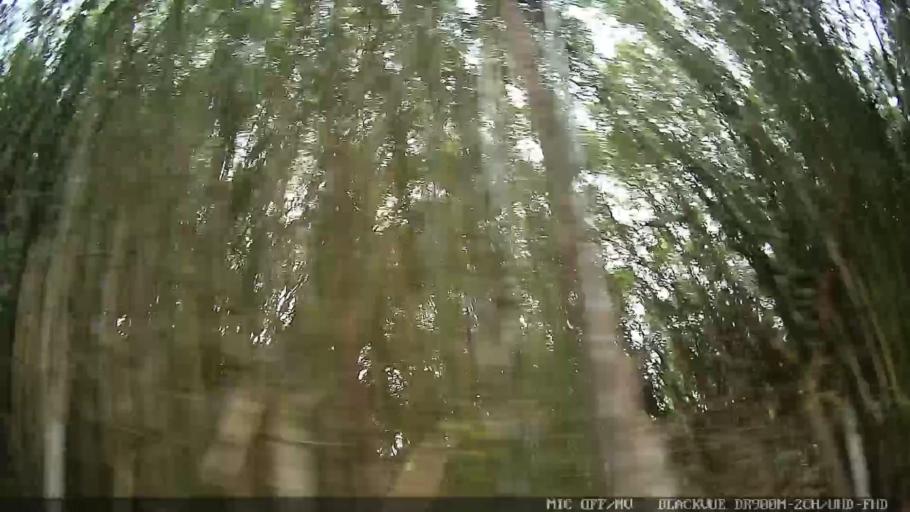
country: BR
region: Sao Paulo
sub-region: Itatiba
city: Itatiba
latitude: -23.0370
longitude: -46.8946
